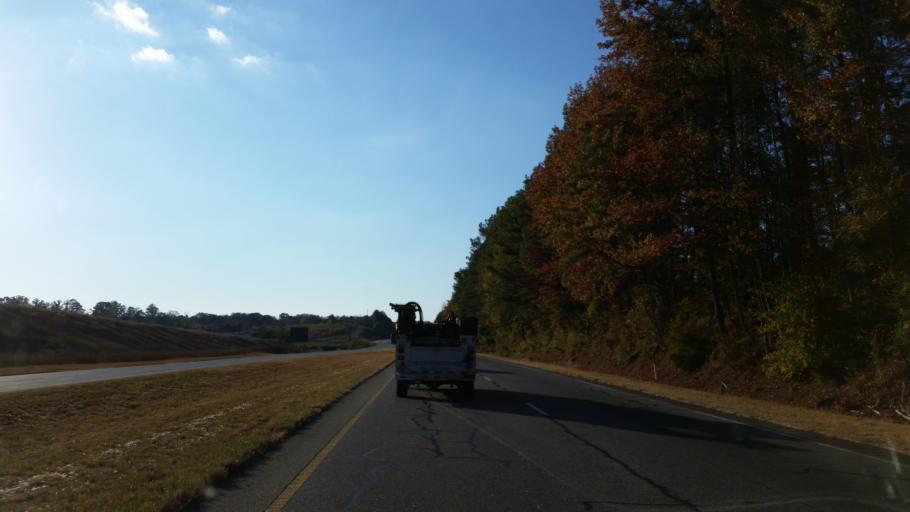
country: US
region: Georgia
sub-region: Bartow County
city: Cartersville
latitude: 34.2181
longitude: -84.8669
